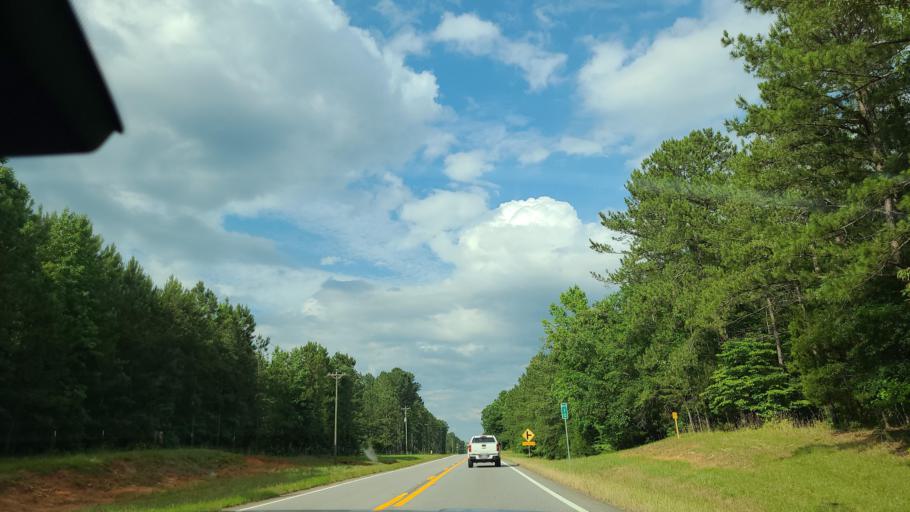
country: US
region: Georgia
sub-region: Jones County
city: Gray
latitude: 33.1543
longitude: -83.4553
